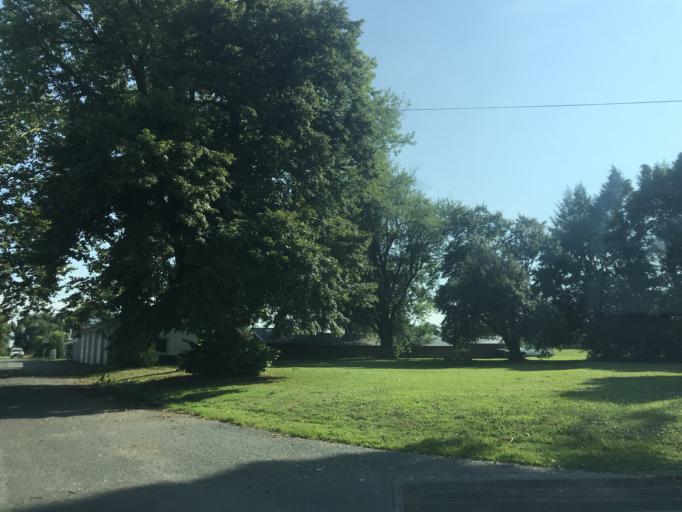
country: US
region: Maryland
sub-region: Harford County
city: Havre de Grace
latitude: 39.5200
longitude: -76.1107
